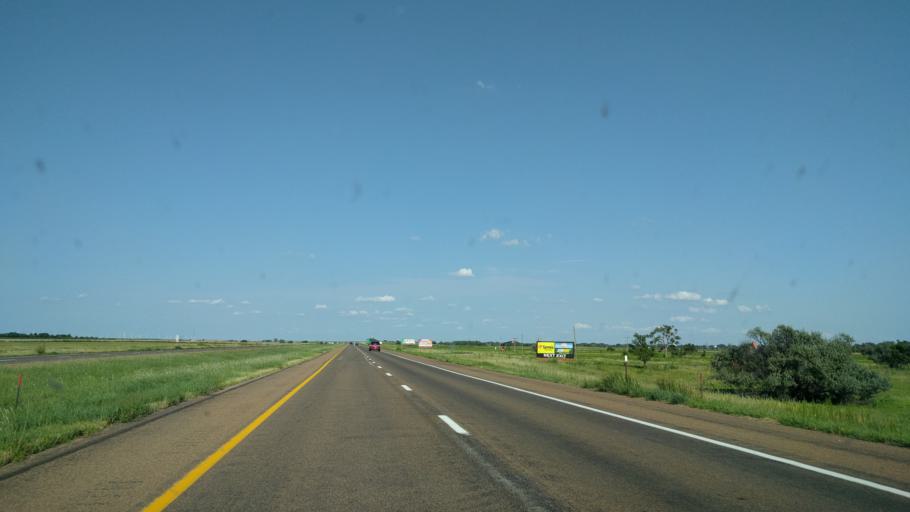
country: US
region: Kansas
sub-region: Ellis County
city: Ellis
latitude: 38.9500
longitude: -99.5915
